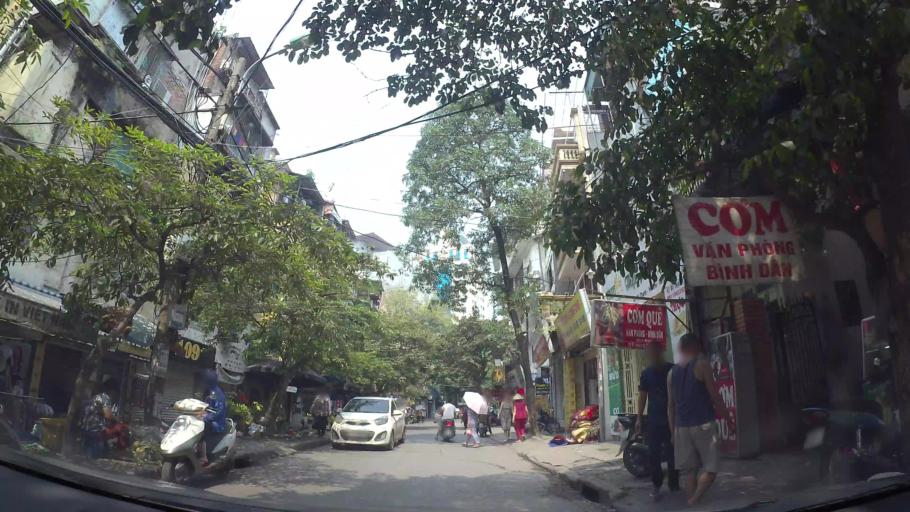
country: VN
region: Ha Noi
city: Dong Da
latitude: 21.0266
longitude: 105.8264
